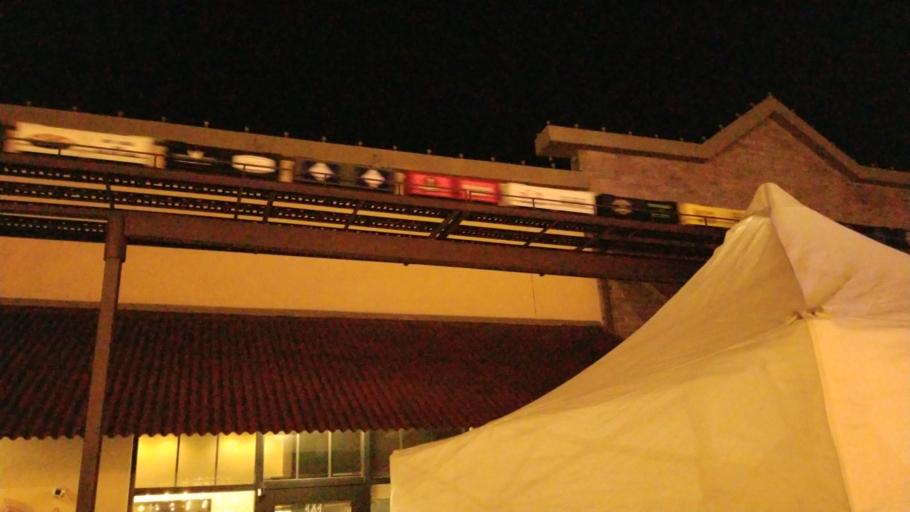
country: US
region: Arizona
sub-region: Maricopa County
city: Carefree
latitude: 33.8299
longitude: -111.9283
